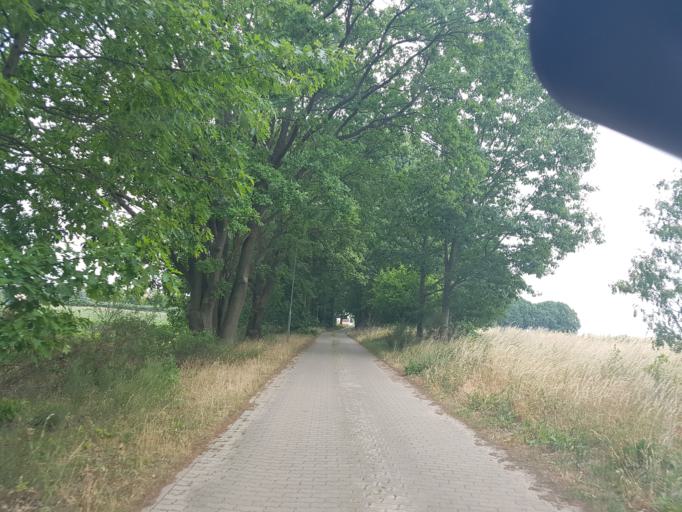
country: DE
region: Brandenburg
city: Treuenbrietzen
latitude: 52.0361
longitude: 12.8112
